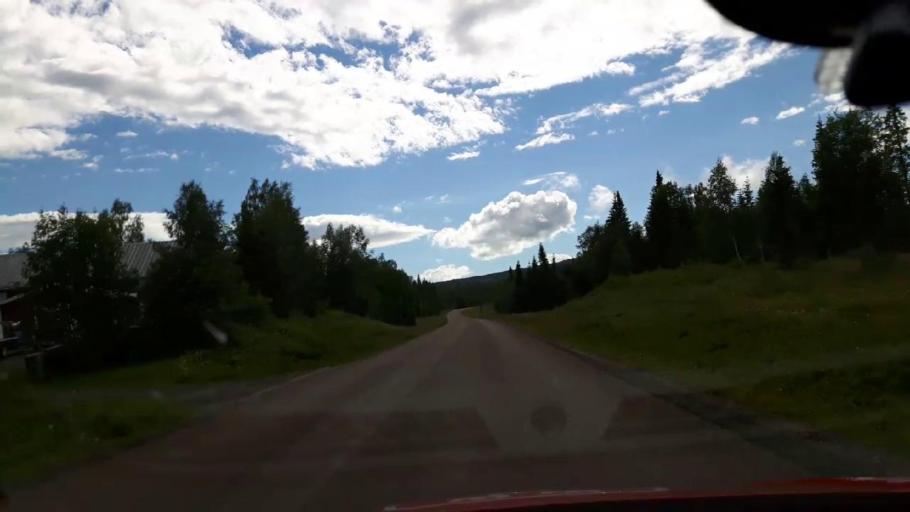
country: SE
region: Jaemtland
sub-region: Are Kommun
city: Are
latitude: 63.3097
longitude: 13.2289
